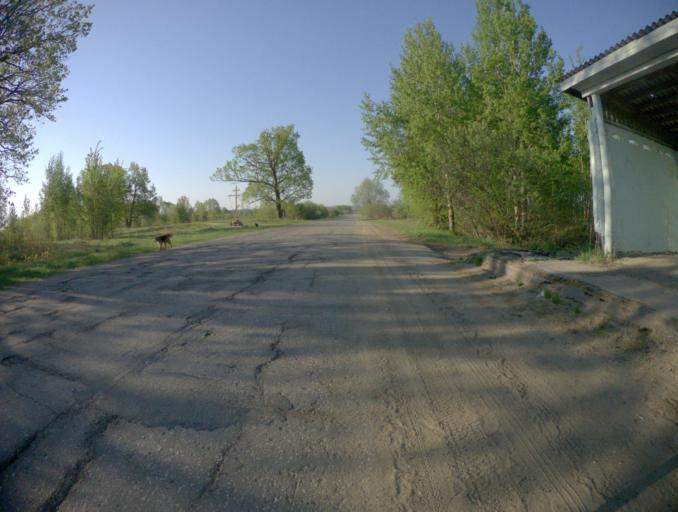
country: RU
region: Vladimir
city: Vyazniki
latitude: 56.2695
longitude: 42.1717
